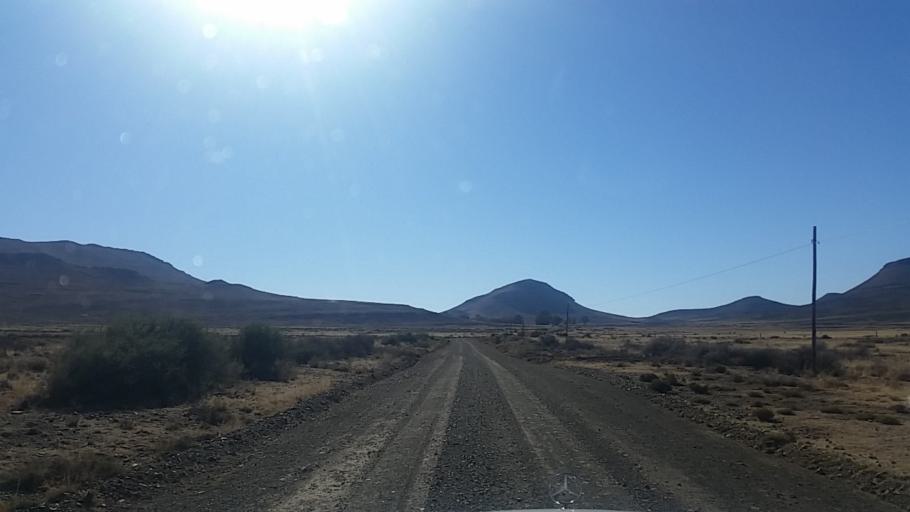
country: ZA
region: Eastern Cape
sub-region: Chris Hani District Municipality
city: Middelburg
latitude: -31.7970
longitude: 24.7137
